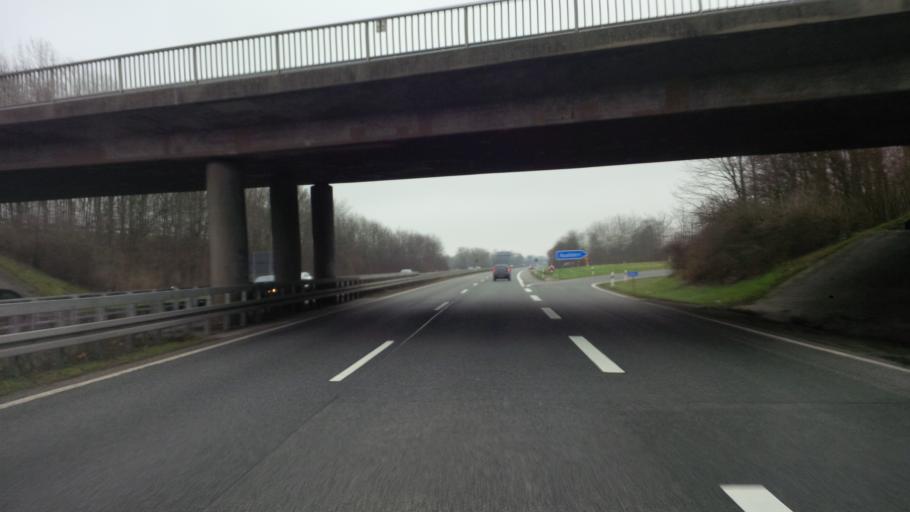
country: DE
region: Hesse
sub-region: Regierungsbezirk Darmstadt
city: Oberursel
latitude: 50.2152
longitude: 8.5765
